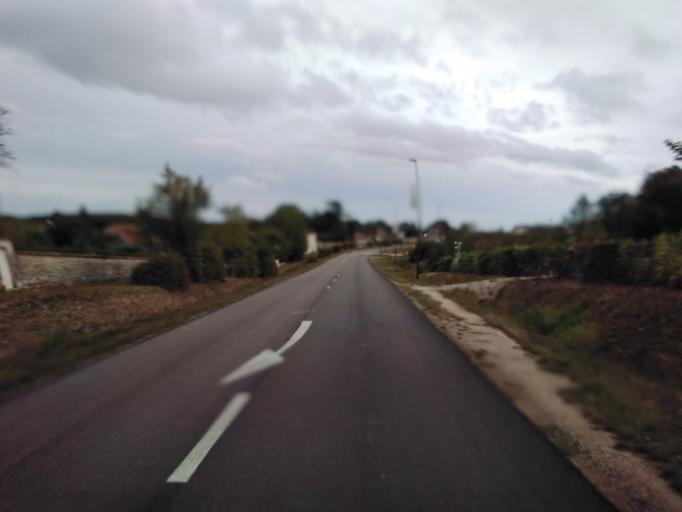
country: FR
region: Champagne-Ardenne
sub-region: Departement de l'Aube
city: Les Riceys
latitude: 47.9885
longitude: 4.3589
